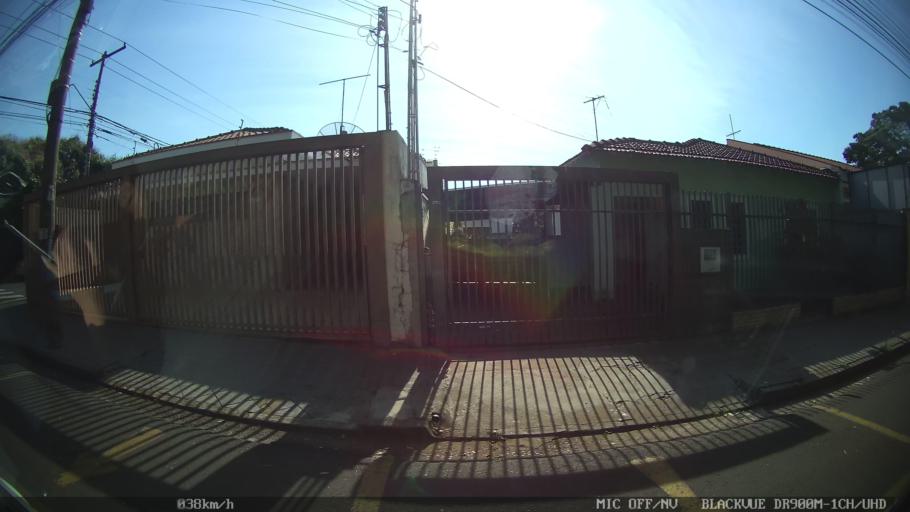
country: BR
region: Sao Paulo
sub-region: Sao Jose Do Rio Preto
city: Sao Jose do Rio Preto
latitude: -20.8047
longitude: -49.3914
